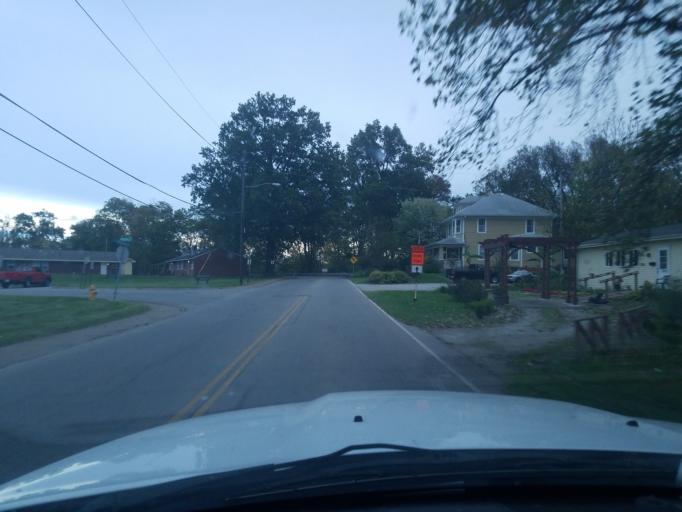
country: US
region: Indiana
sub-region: Floyd County
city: New Albany
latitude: 38.2959
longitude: -85.8258
